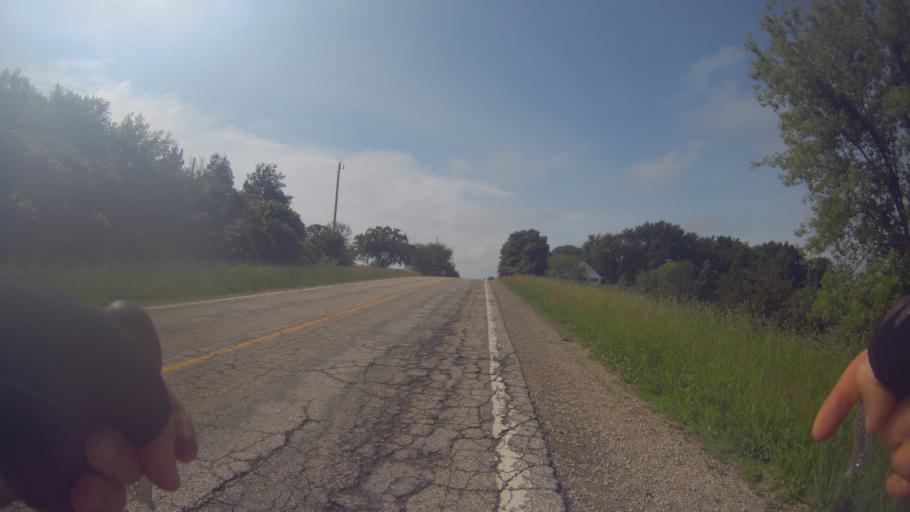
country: US
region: Wisconsin
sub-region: Dane County
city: Stoughton
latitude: 42.9638
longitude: -89.1809
